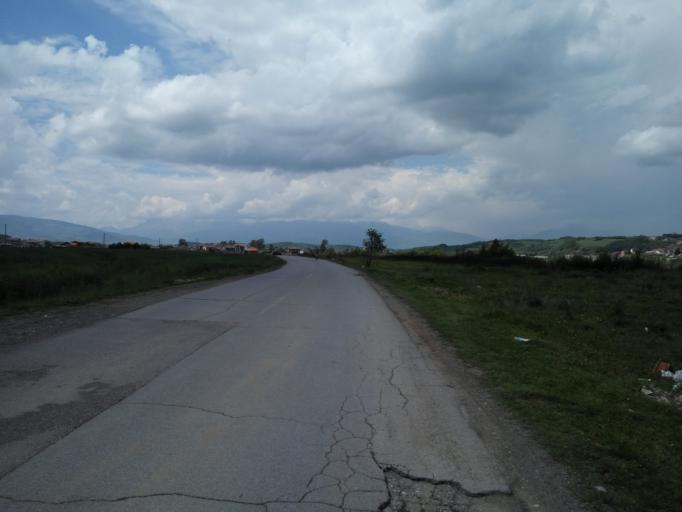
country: XK
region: Gjakova
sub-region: Komuna e Gjakoves
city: Gjakove
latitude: 42.3629
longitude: 20.4297
